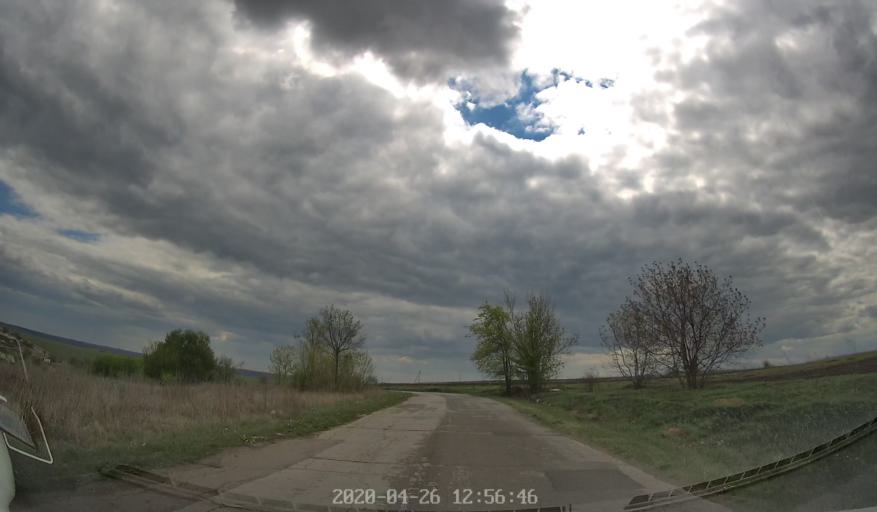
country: MD
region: Chisinau
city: Vadul lui Voda
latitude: 47.0706
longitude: 29.0673
